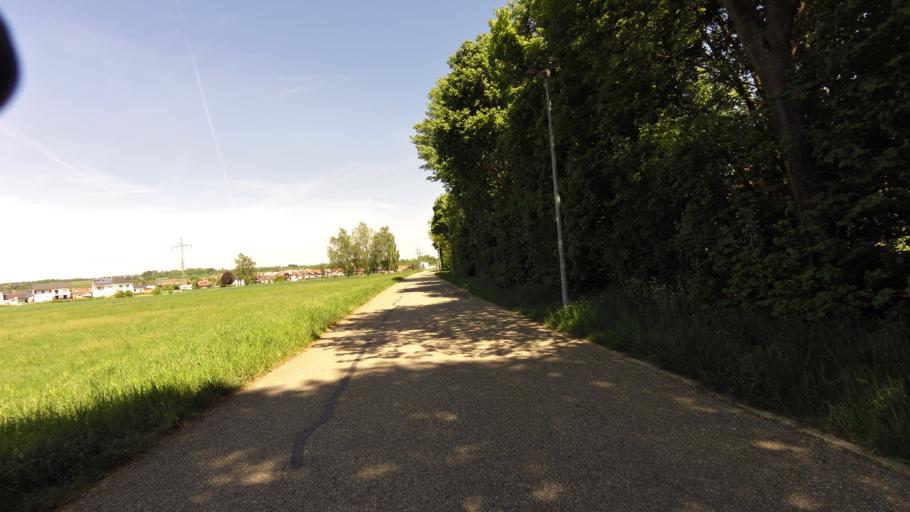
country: DE
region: Bavaria
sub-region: Lower Bavaria
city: Landshut
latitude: 48.5493
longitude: 12.1154
